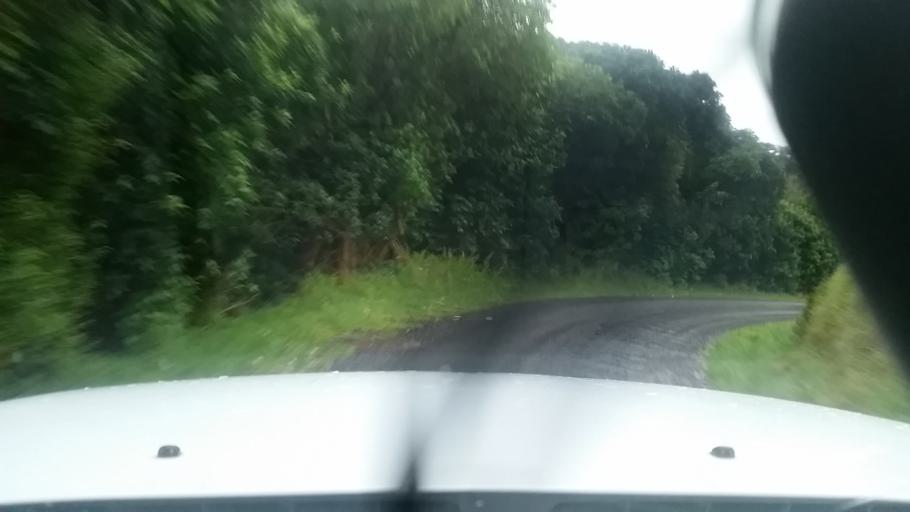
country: NZ
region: Canterbury
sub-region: Christchurch City
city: Christchurch
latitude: -43.8104
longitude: 172.8848
